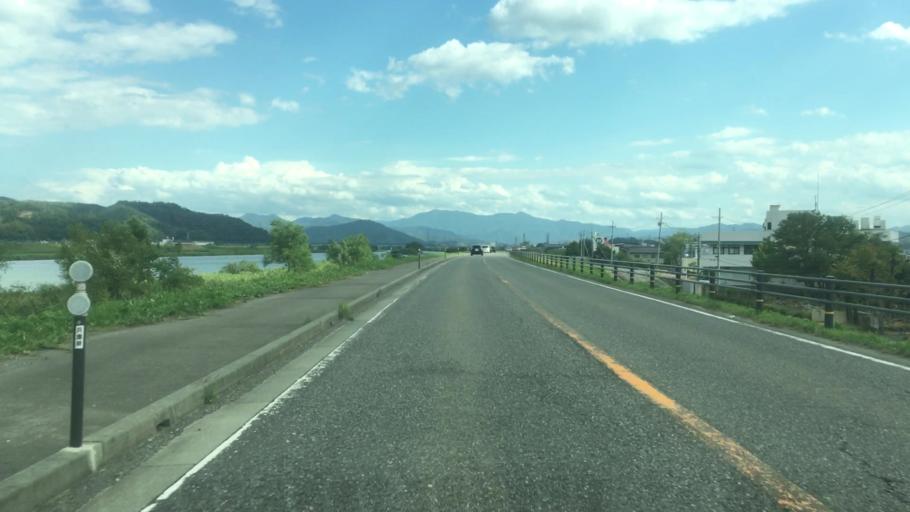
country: JP
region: Hyogo
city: Toyooka
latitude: 35.5721
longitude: 134.8076
